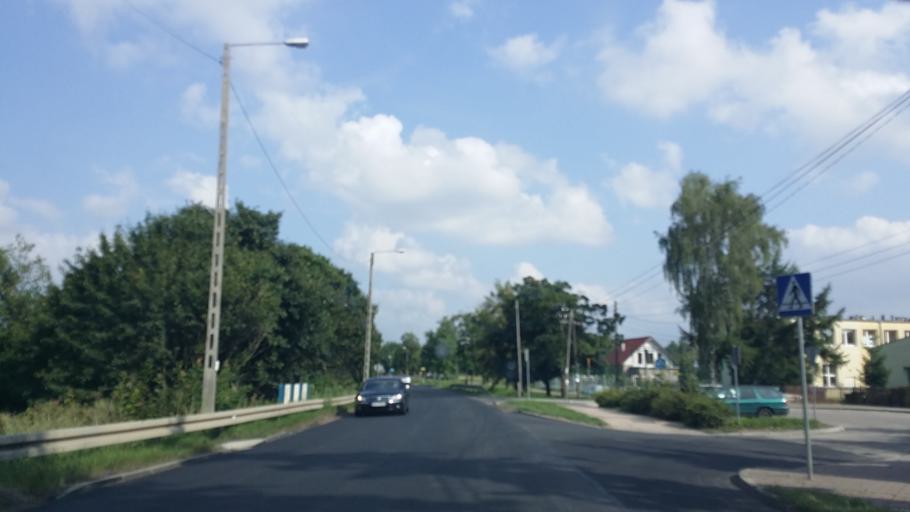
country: PL
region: Lubusz
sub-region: Powiat gorzowski
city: Klodawa
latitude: 52.7828
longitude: 15.2191
